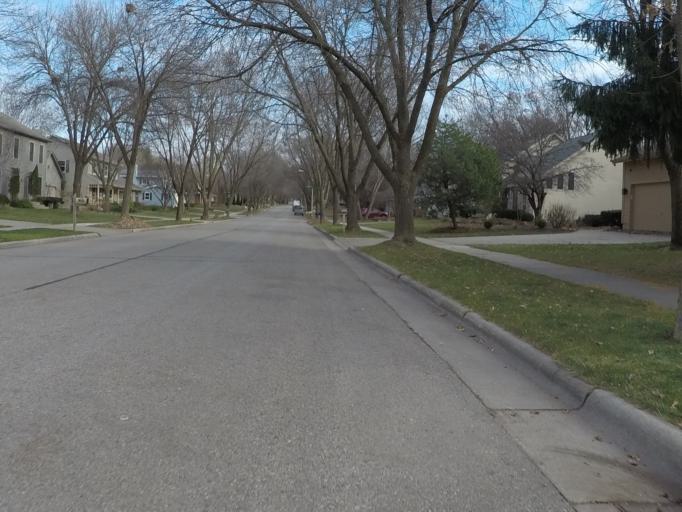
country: US
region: Wisconsin
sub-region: Dane County
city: Middleton
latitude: 43.0723
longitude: -89.5159
